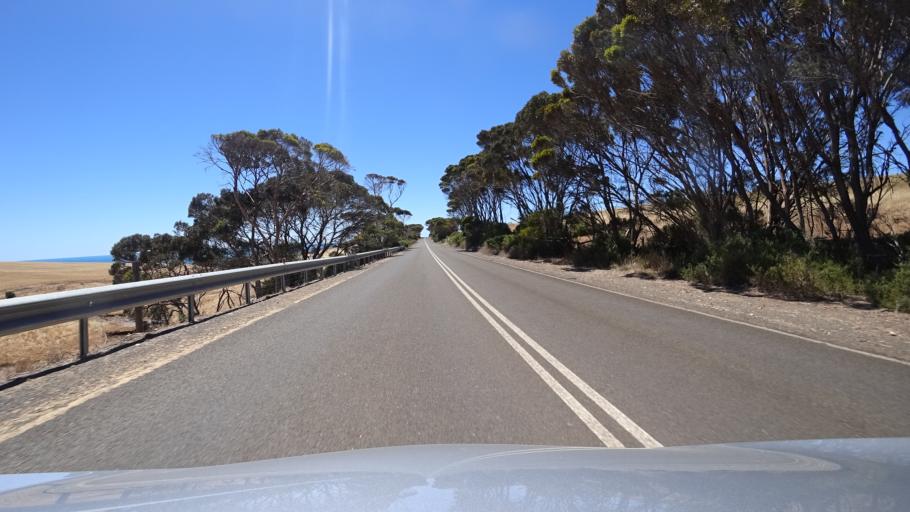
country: AU
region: South Australia
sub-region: Kangaroo Island
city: Kingscote
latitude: -35.7333
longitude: 137.9319
